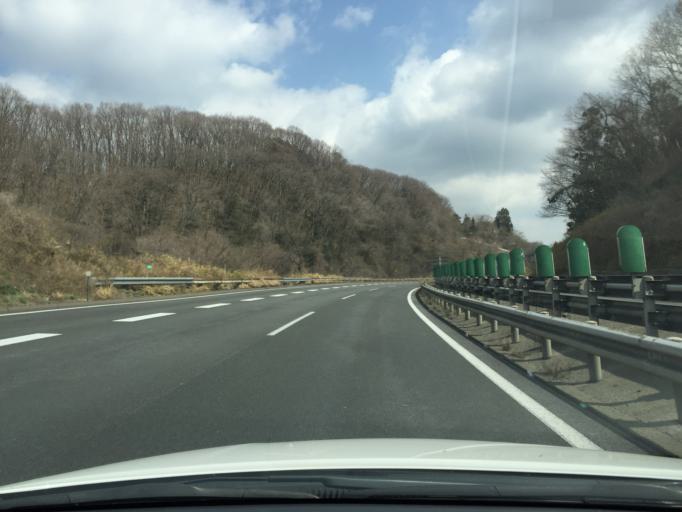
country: JP
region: Miyagi
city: Sendai
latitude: 38.2271
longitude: 140.8039
